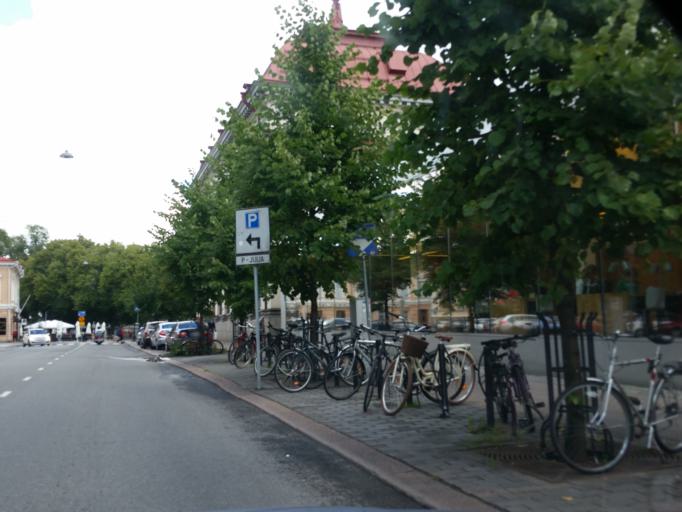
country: FI
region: Varsinais-Suomi
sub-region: Turku
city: Turku
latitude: 60.4508
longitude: 22.2713
